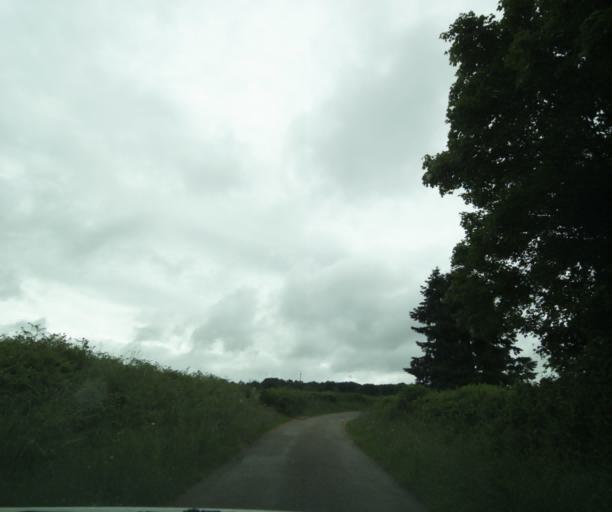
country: FR
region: Bourgogne
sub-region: Departement de Saone-et-Loire
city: Charolles
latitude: 46.4968
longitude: 4.2817
